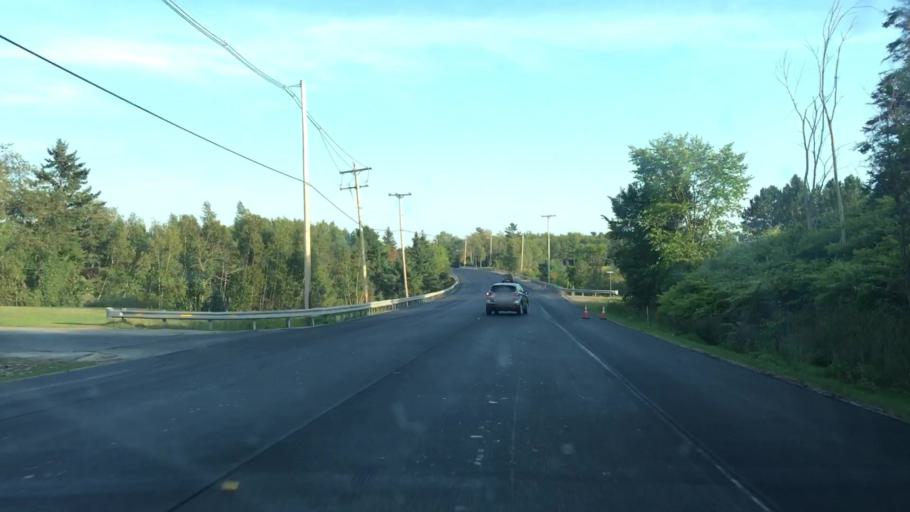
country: US
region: Maine
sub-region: Penobscot County
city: Hampden
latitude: 44.7696
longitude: -68.8566
